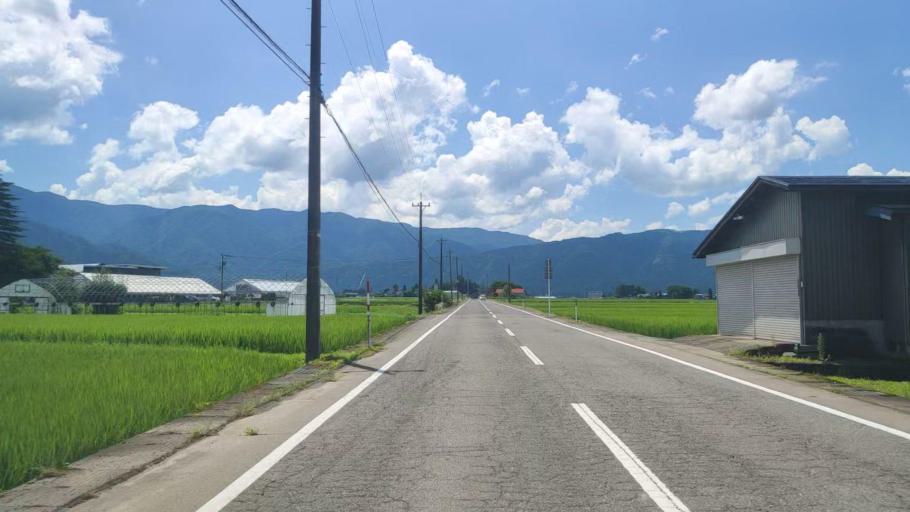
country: JP
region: Fukui
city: Ono
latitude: 35.9679
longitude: 136.5280
